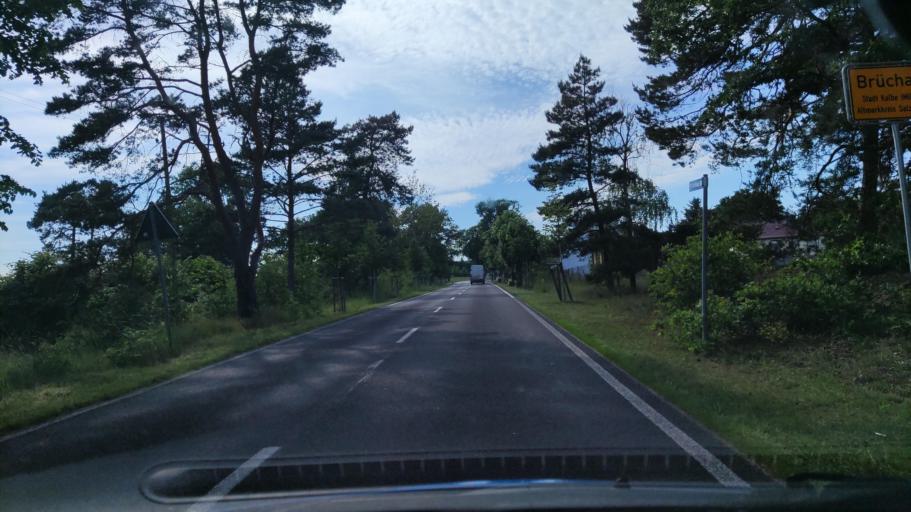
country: DE
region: Saxony-Anhalt
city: Klotze
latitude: 52.6867
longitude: 11.2522
